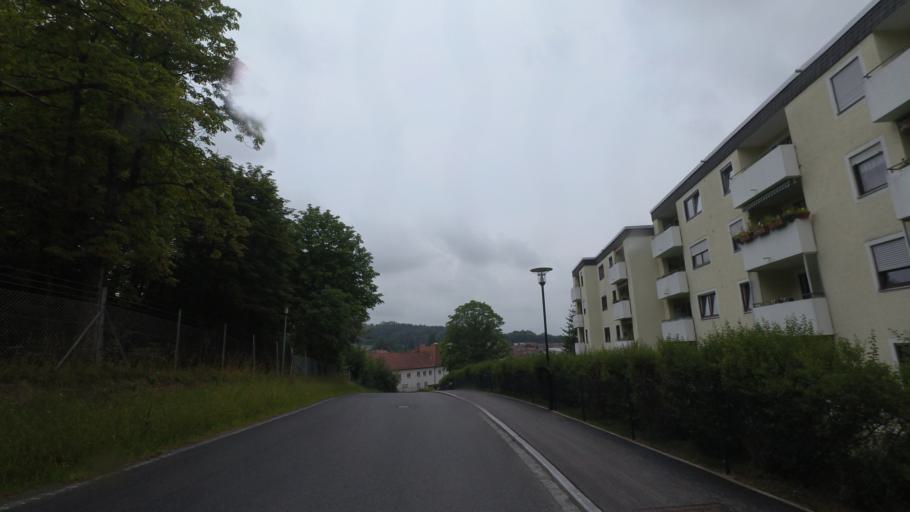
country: DE
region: Bavaria
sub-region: Upper Bavaria
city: Traunstein
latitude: 47.8653
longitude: 12.6321
